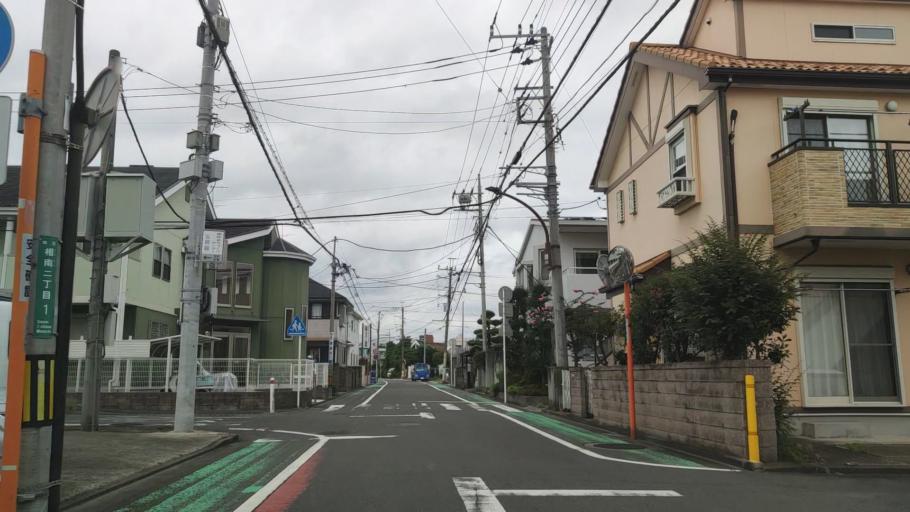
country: JP
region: Tokyo
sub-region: Machida-shi
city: Machida
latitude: 35.5169
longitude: 139.4355
